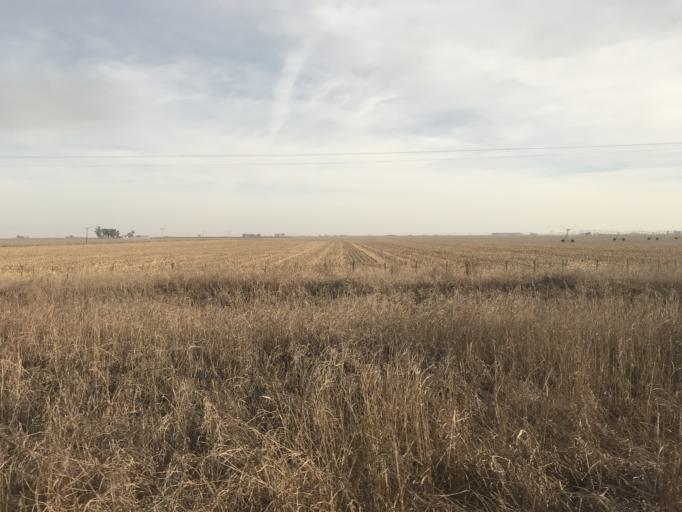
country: AR
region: Cordoba
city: Pilar
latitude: -31.7276
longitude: -63.8461
